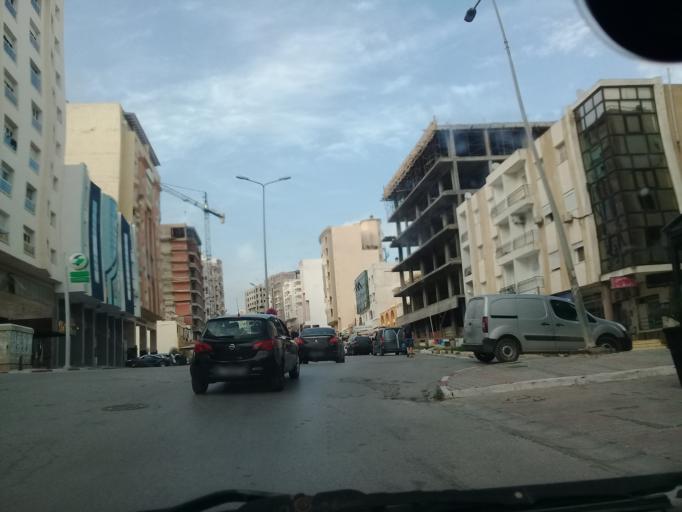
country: TN
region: Ariana
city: Ariana
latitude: 36.8659
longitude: 10.1692
